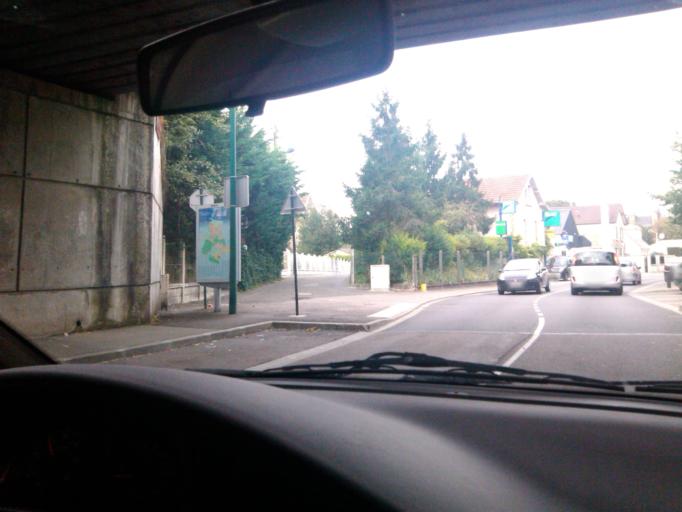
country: FR
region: Ile-de-France
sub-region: Departement des Yvelines
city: Plaisir
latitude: 48.8321
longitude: 1.9415
